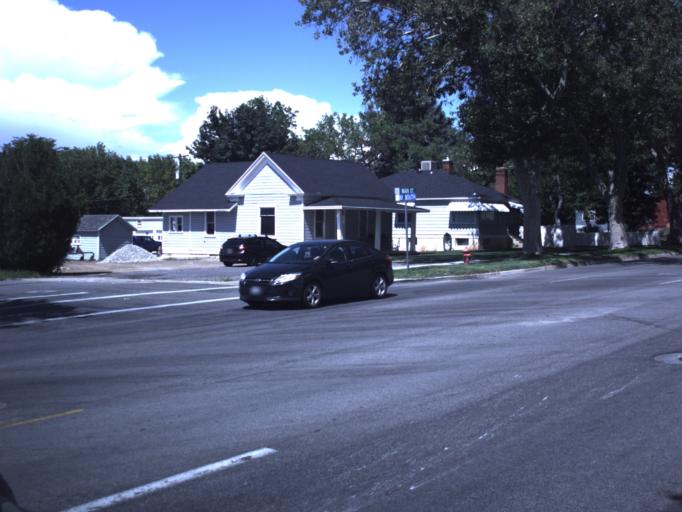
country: US
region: Utah
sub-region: Box Elder County
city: Brigham City
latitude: 41.4982
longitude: -112.0159
